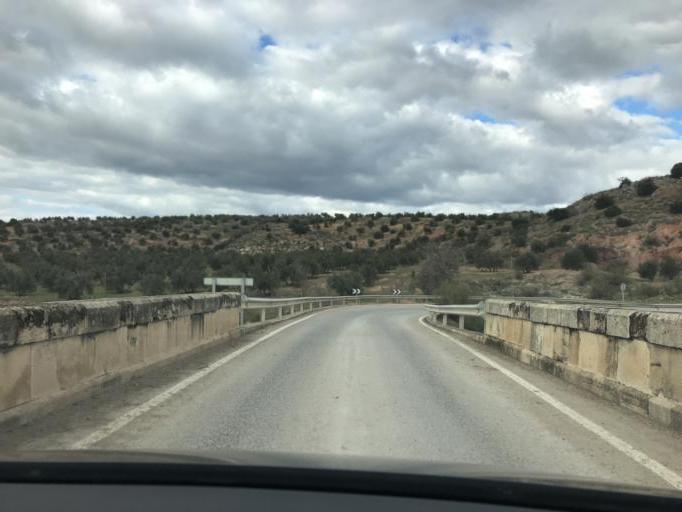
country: ES
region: Andalusia
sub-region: Provincia de Jaen
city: Baeza
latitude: 37.9280
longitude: -3.4539
